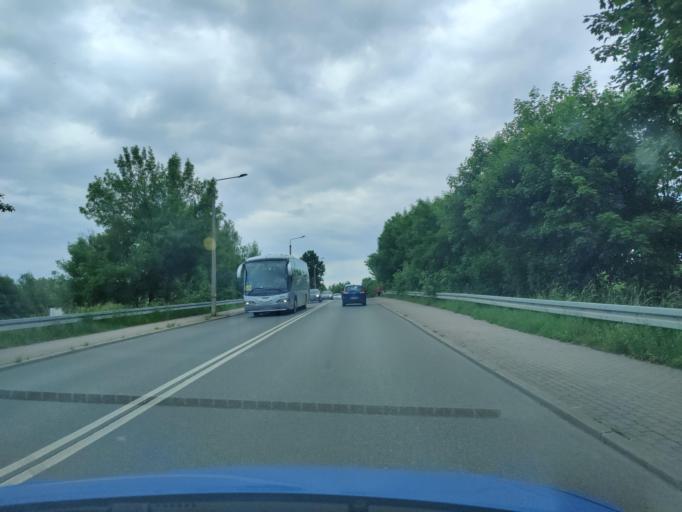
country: PL
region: Silesian Voivodeship
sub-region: Sosnowiec
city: Sosnowiec
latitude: 50.2647
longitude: 19.1485
